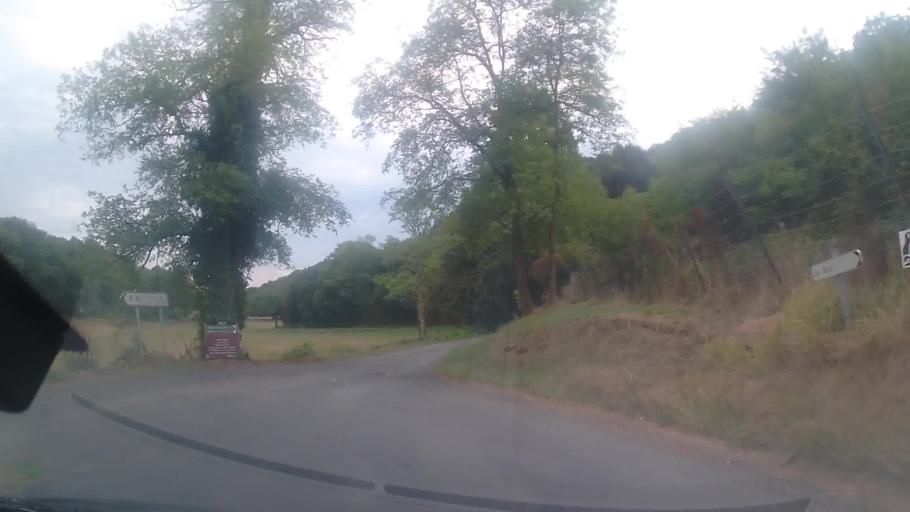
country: FR
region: Aquitaine
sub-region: Departement de la Dordogne
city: Eyvigues-et-Eybenes
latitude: 44.8415
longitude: 1.3520
